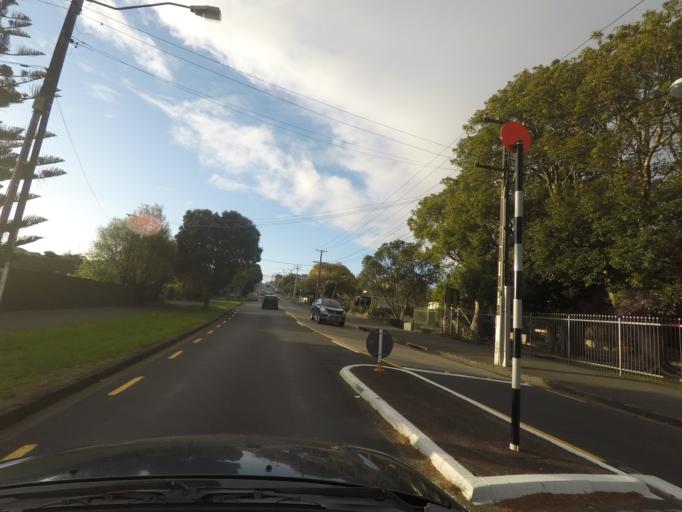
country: NZ
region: Auckland
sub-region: Auckland
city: Waitakere
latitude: -36.9101
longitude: 174.7018
